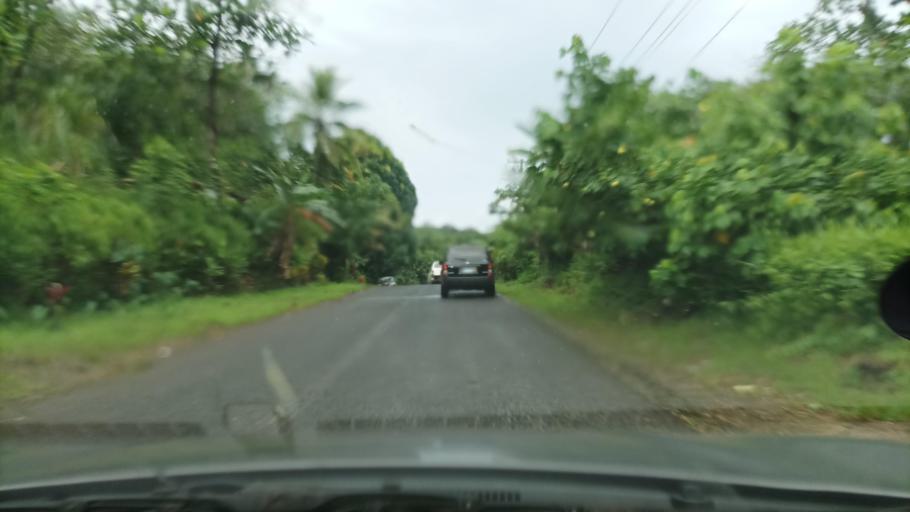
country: FM
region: Pohnpei
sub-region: Sokehs Municipality
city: Palikir - National Government Center
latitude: 6.8467
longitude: 158.1589
